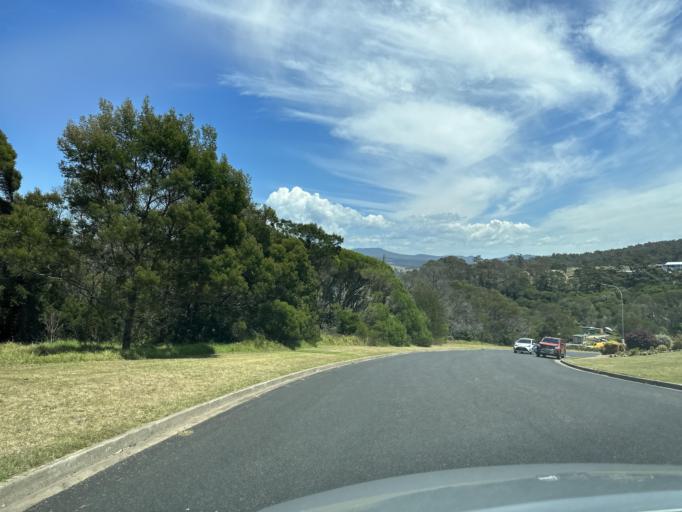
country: AU
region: New South Wales
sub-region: Bega Valley
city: Merimbula
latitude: -36.8921
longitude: 149.8937
